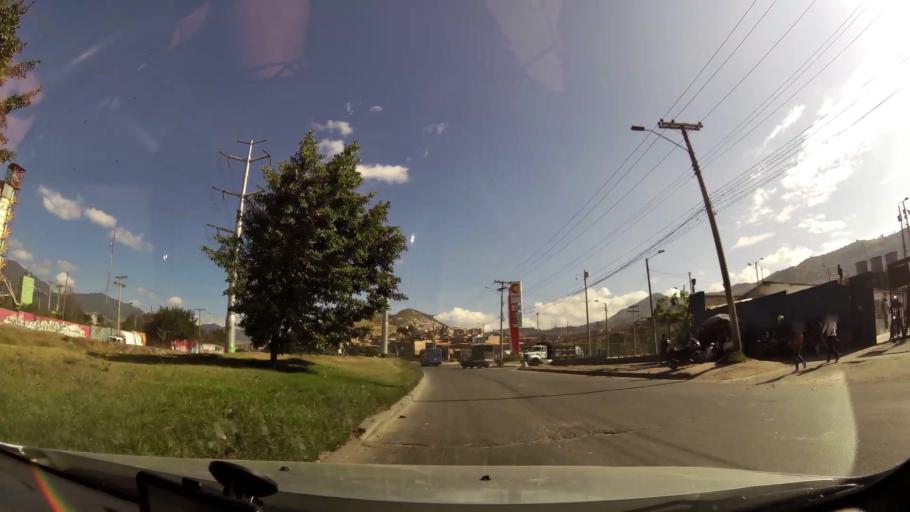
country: CO
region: Bogota D.C.
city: Bogota
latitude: 4.5479
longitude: -74.1372
